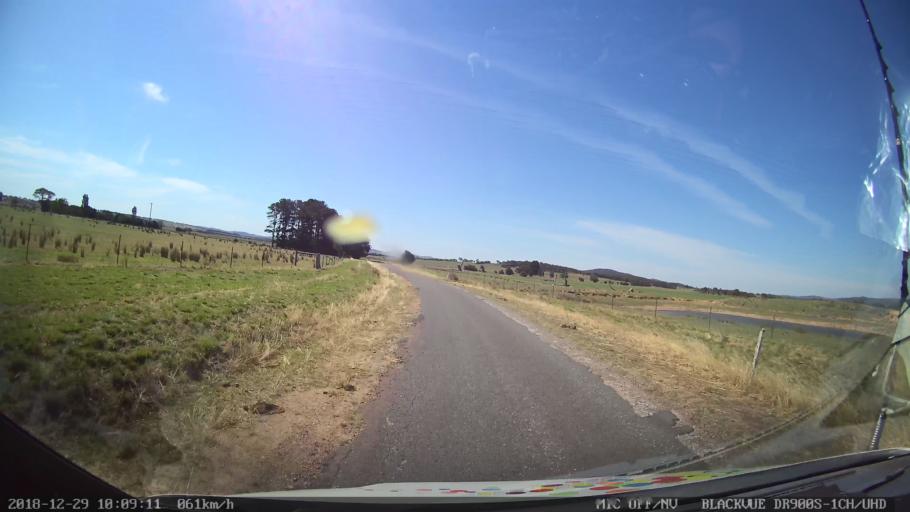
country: AU
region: New South Wales
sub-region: Yass Valley
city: Gundaroo
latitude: -34.8634
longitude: 149.4589
